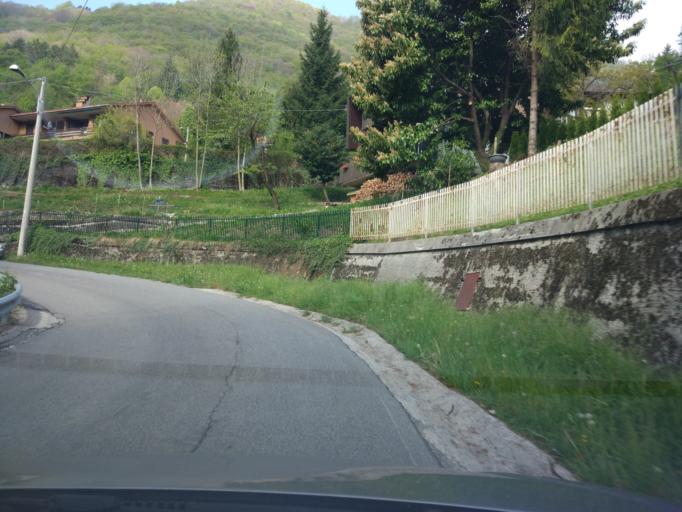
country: IT
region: Lombardy
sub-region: Provincia di Lecco
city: Ballabio
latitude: 45.9004
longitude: 9.4162
